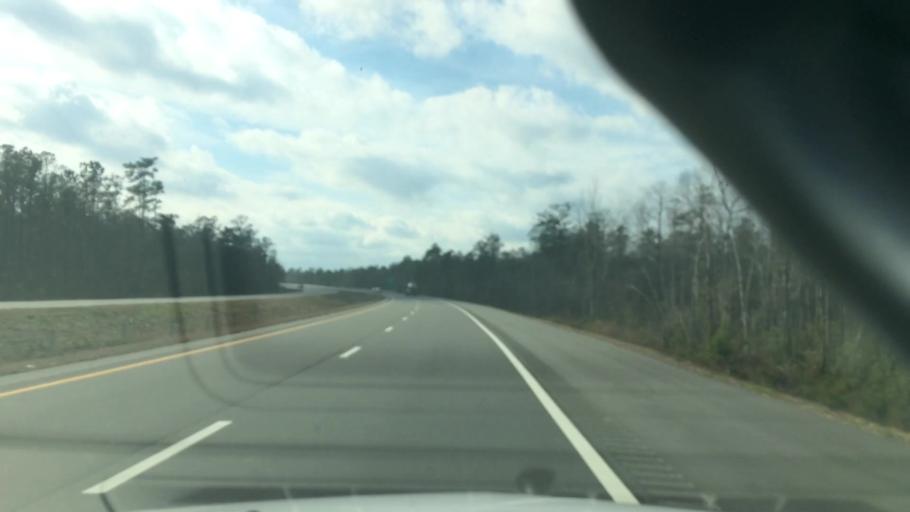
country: US
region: North Carolina
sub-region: Brunswick County
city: Leland
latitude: 34.2787
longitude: -78.0669
